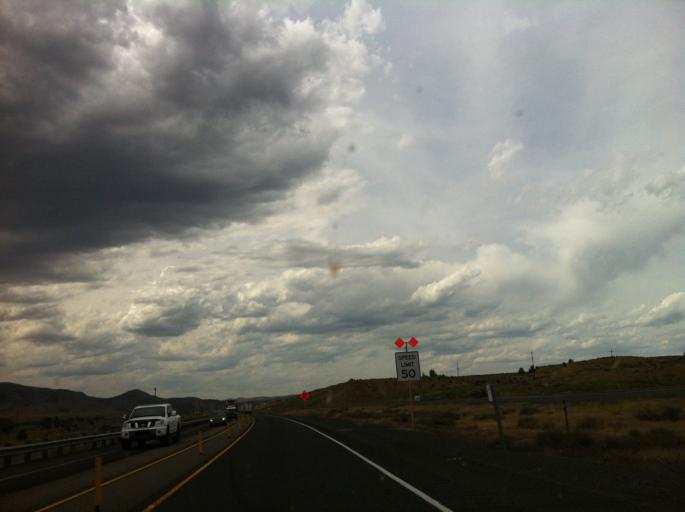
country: US
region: Oregon
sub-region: Baker County
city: Baker City
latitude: 44.5559
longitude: -117.4264
